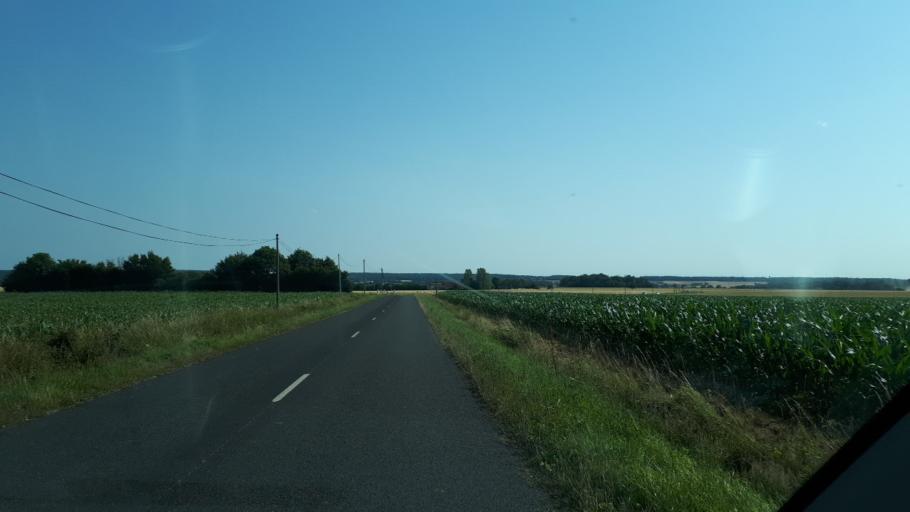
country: FR
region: Centre
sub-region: Departement du Loir-et-Cher
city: Droue
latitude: 48.0521
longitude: 1.1004
